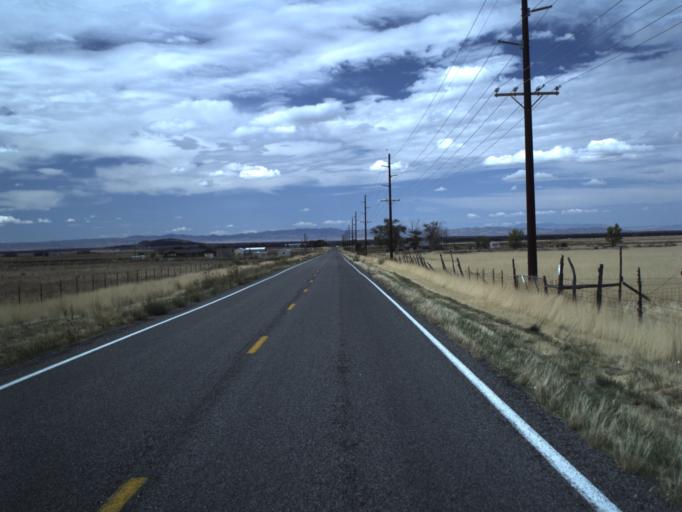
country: US
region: Utah
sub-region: Millard County
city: Fillmore
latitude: 38.9792
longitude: -112.3953
